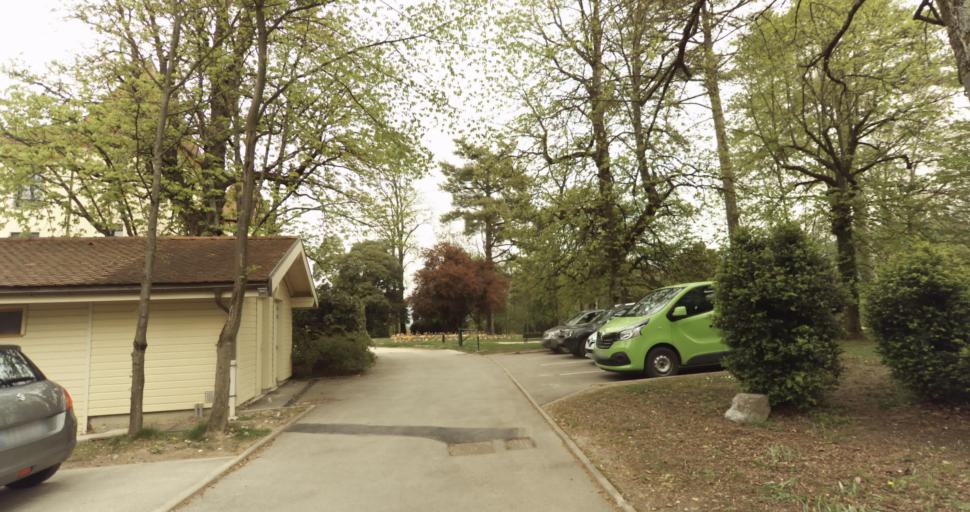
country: FR
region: Rhone-Alpes
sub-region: Departement de l'Isere
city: Montbonnot-Saint-Martin
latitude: 45.2252
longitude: 5.8013
